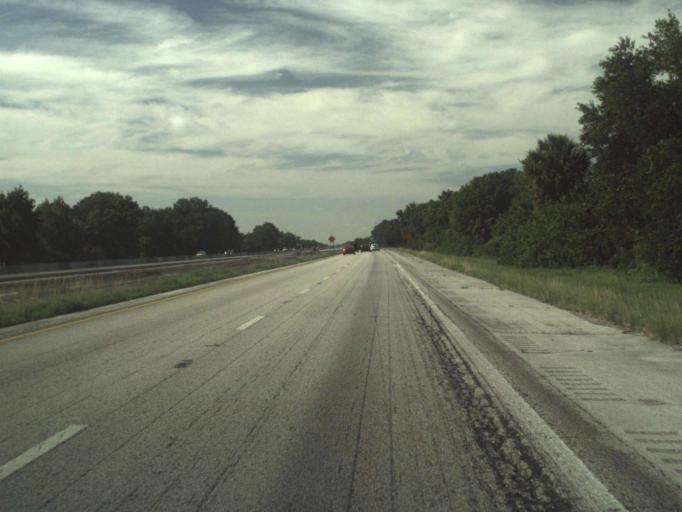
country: US
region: Florida
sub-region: Indian River County
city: Fellsmere
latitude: 27.7417
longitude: -80.5496
